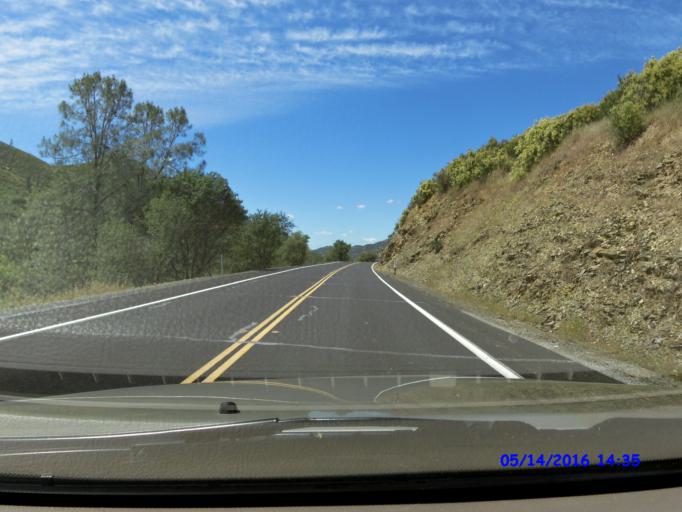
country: US
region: California
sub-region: Tuolumne County
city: Tuolumne City
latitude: 37.7794
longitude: -120.2722
